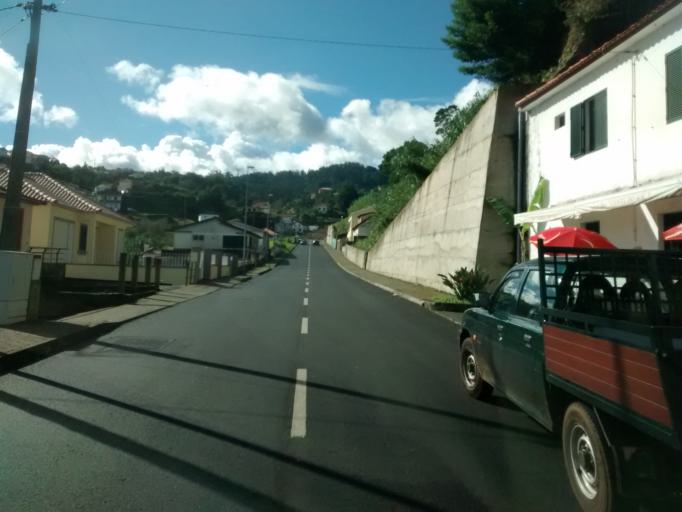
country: PT
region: Madeira
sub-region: Santana
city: Santana
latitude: 32.8078
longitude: -16.8847
